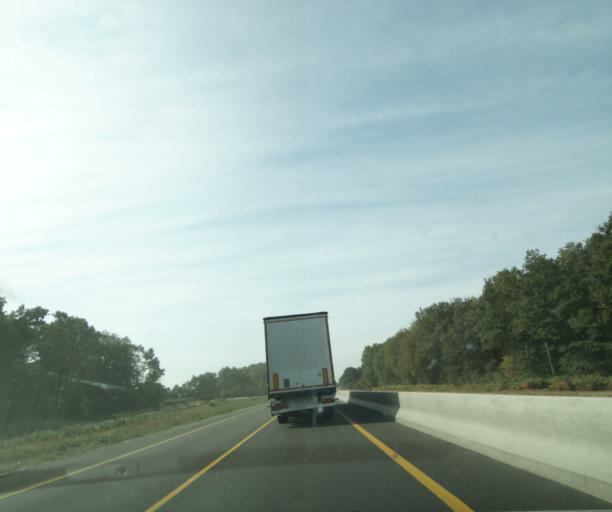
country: FR
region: Bourgogne
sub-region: Departement de Saone-et-Loire
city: Paray-le-Monial
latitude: 46.4871
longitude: 4.1522
